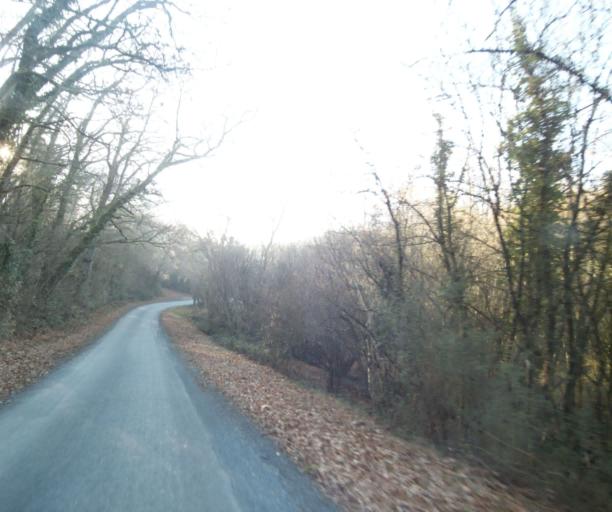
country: FR
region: Poitou-Charentes
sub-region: Departement de la Charente-Maritime
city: Fontcouverte
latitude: 45.7578
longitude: -0.6080
